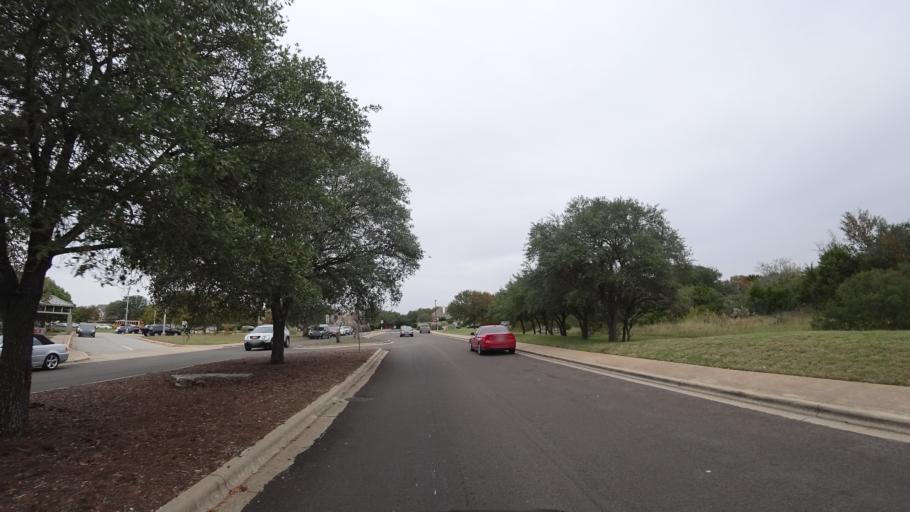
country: US
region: Texas
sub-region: Travis County
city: Shady Hollow
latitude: 30.1912
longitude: -97.8803
